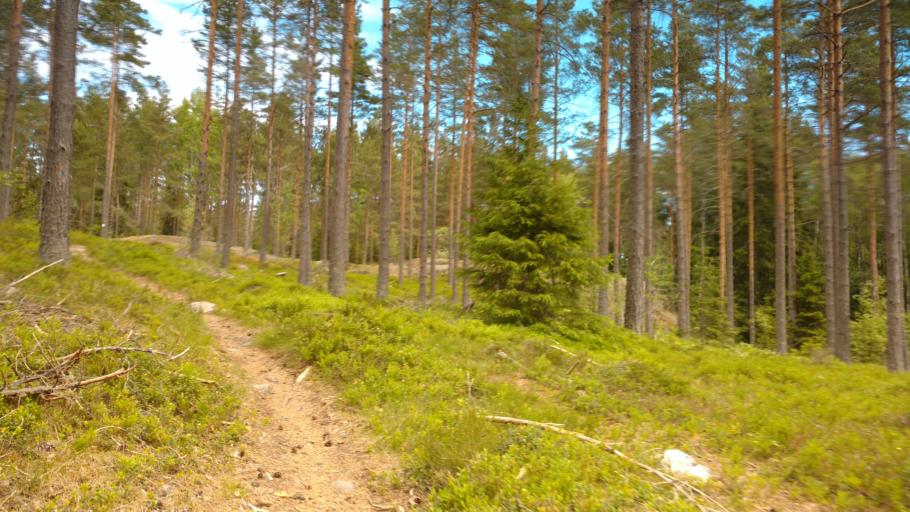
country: FI
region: Uusimaa
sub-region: Raaseporin
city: Pohja
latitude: 60.1103
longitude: 23.5602
